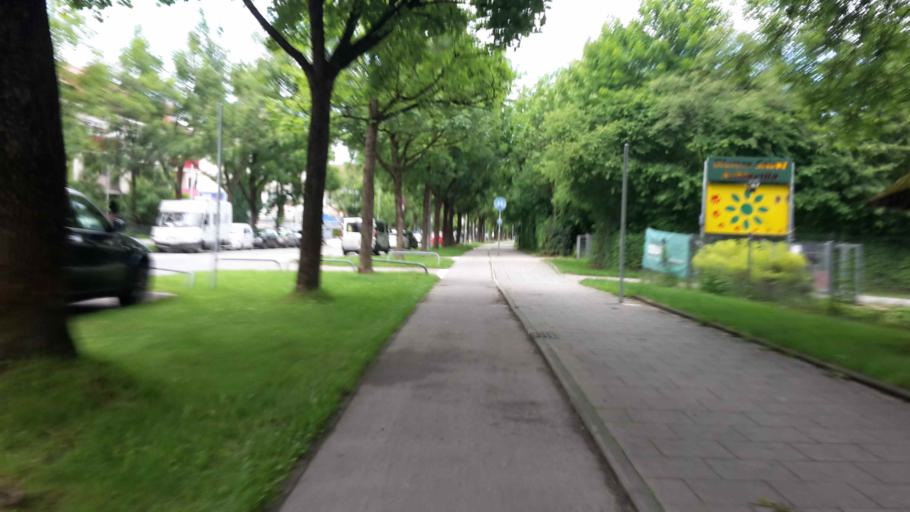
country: DE
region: Bavaria
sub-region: Upper Bavaria
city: Munich
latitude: 48.1041
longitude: 11.5620
